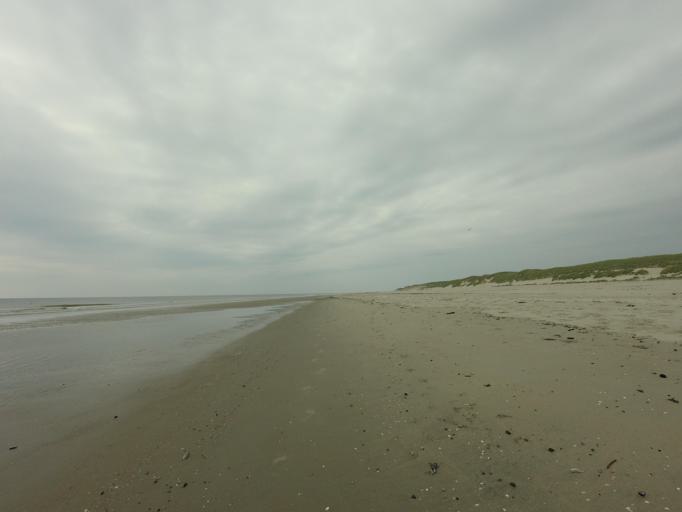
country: NL
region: North Holland
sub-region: Gemeente Den Helder
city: Den Helder
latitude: 53.0076
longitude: 4.7105
